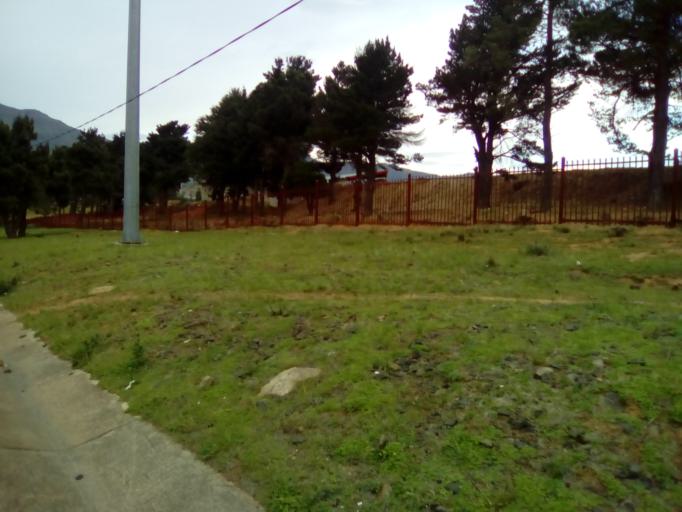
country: LS
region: Qacha's Nek
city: Qacha's Nek
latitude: -30.1113
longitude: 28.6813
